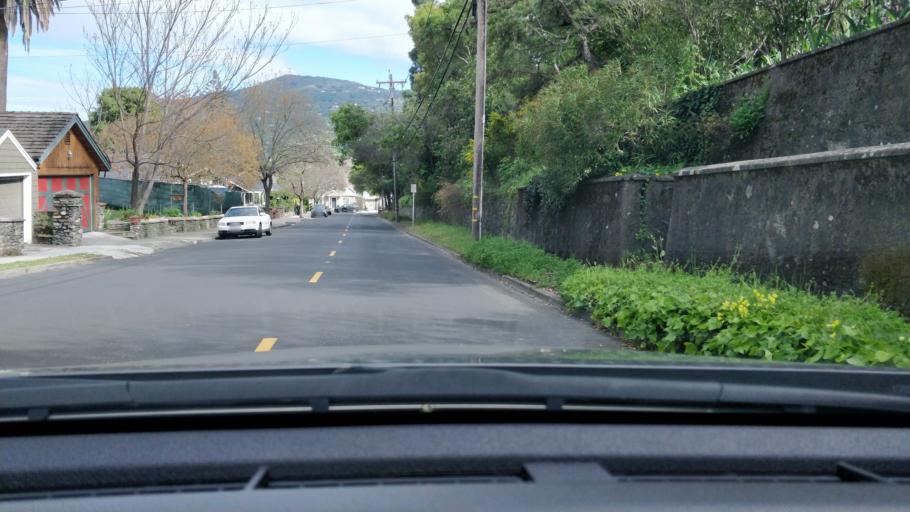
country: US
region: California
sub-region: Santa Clara County
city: Monte Sereno
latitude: 37.2248
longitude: -121.9877
